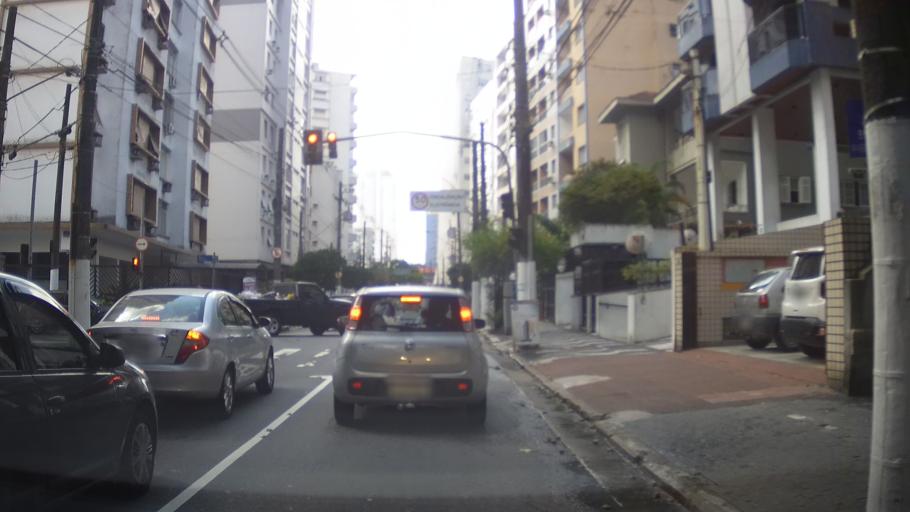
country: BR
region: Sao Paulo
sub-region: Santos
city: Santos
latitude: -23.9698
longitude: -46.3257
